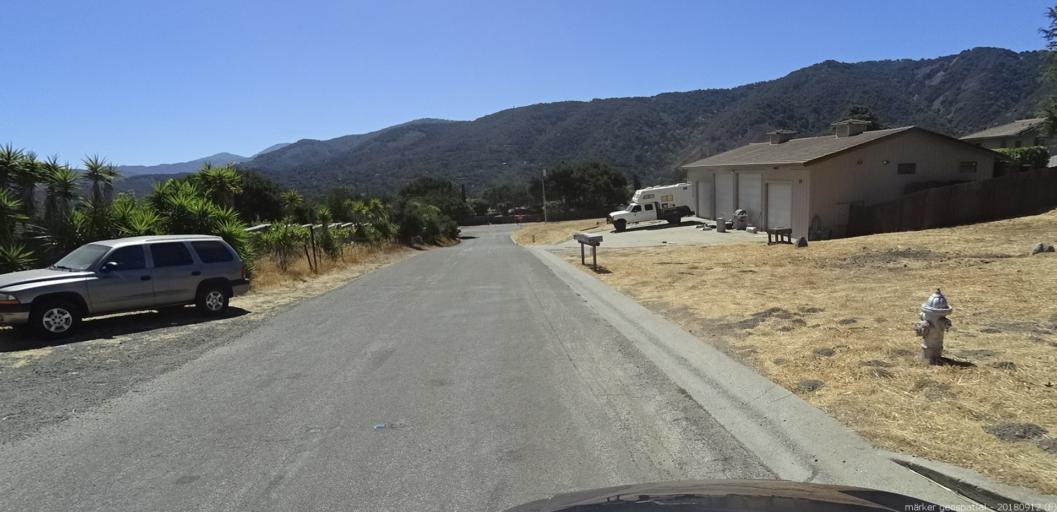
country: US
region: California
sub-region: Monterey County
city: Carmel Valley Village
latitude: 36.4850
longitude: -121.7314
